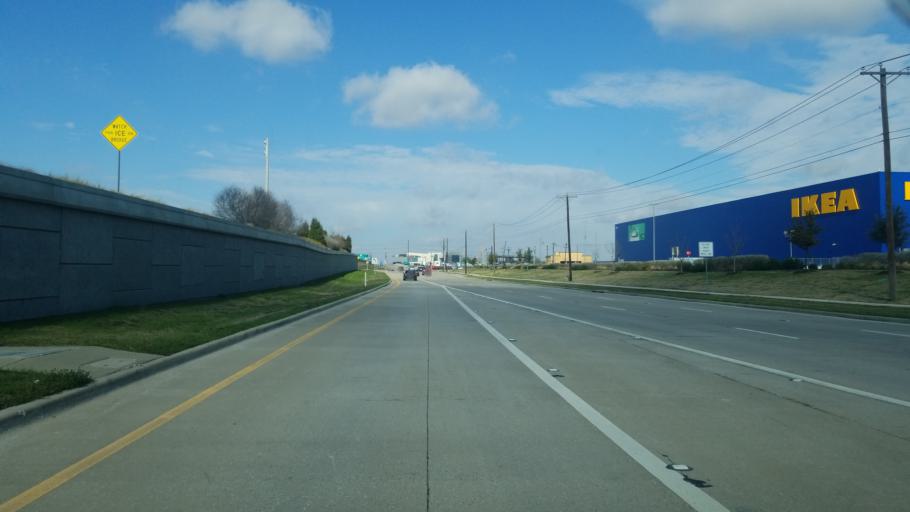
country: US
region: Texas
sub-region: Dallas County
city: Grand Prairie
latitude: 32.6891
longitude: -97.0239
